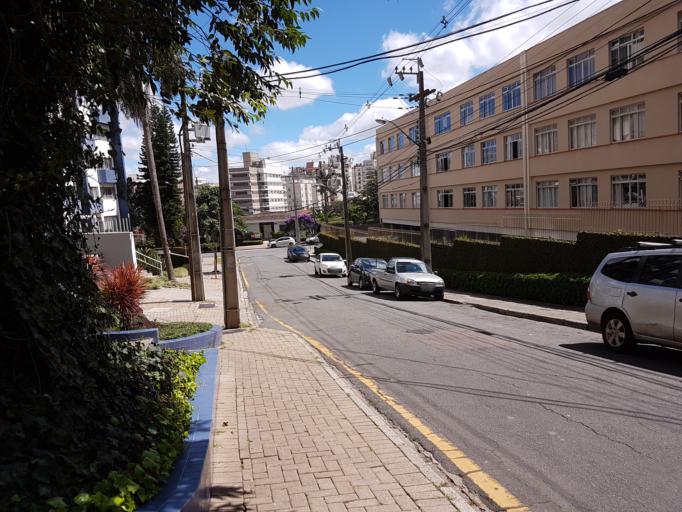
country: BR
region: Parana
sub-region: Curitiba
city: Curitiba
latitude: -25.4358
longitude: -49.2416
